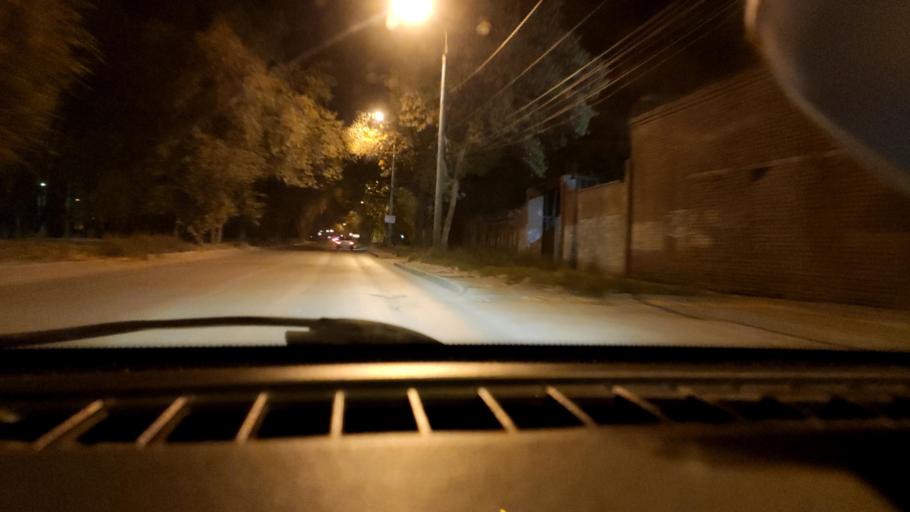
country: RU
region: Samara
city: Petra-Dubrava
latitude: 53.2295
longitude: 50.2912
